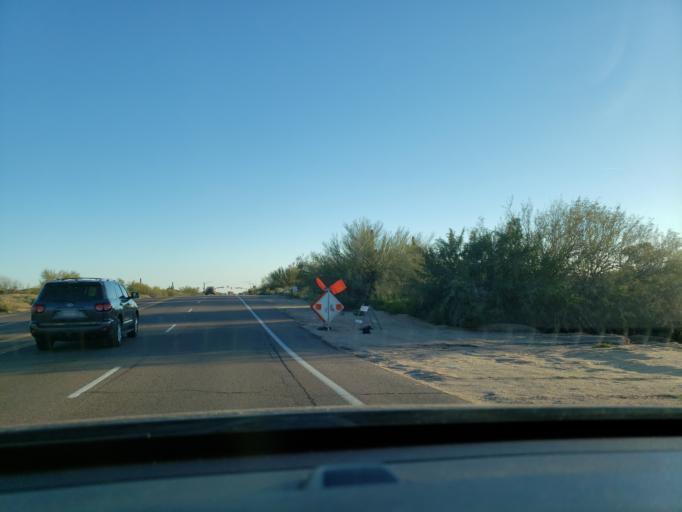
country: US
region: Arizona
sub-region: Maricopa County
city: Carefree
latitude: 33.7740
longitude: -111.9260
